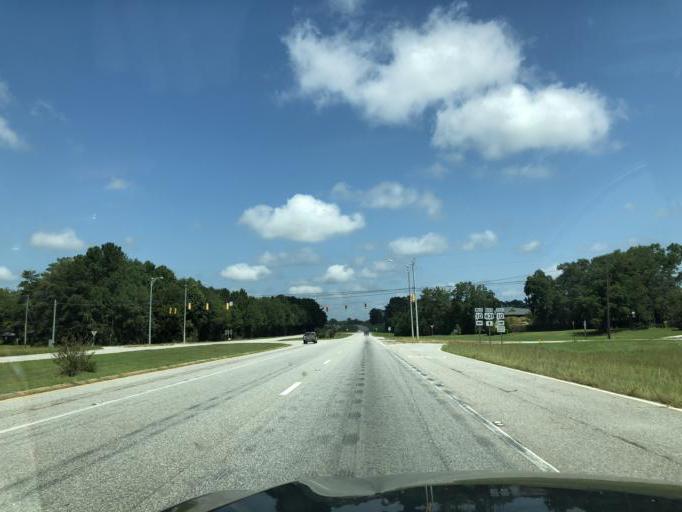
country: US
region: Alabama
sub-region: Henry County
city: Abbeville
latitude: 31.5878
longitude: -85.2786
